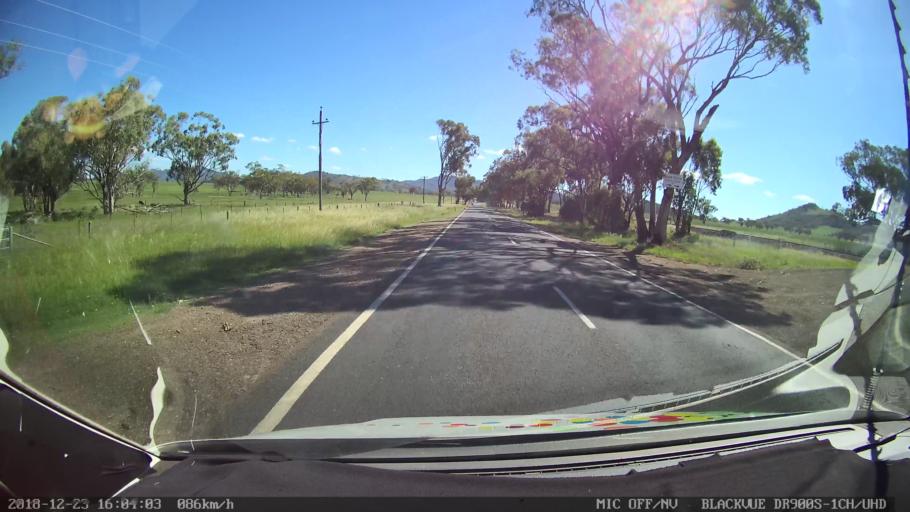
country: AU
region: New South Wales
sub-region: Tamworth Municipality
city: Phillip
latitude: -31.2503
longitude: 150.7956
